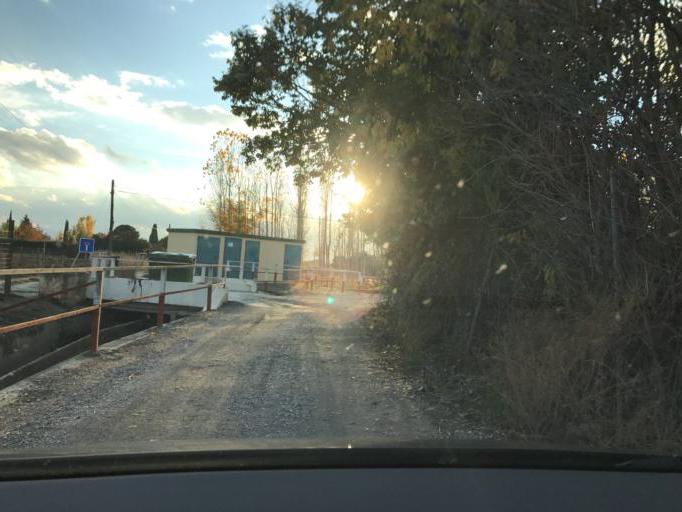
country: ES
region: Andalusia
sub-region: Provincia de Granada
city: Granada
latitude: 37.1676
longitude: -3.6143
